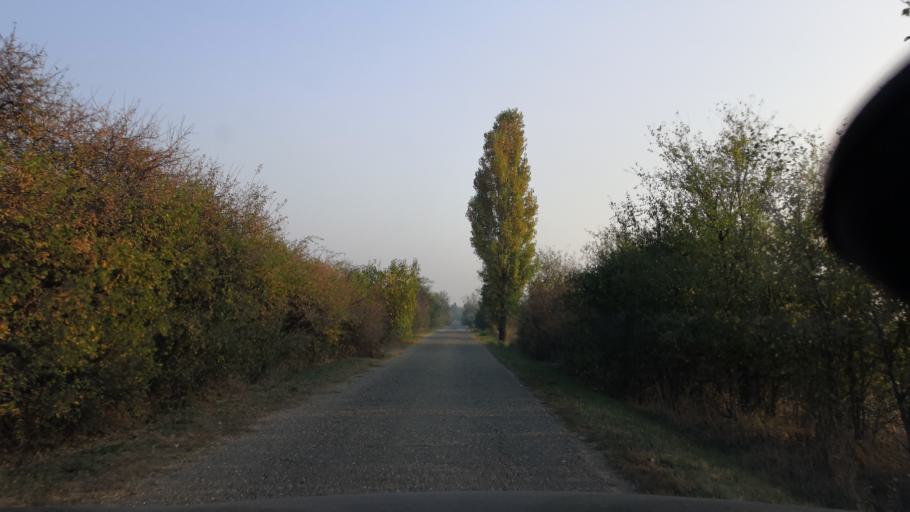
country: RS
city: Cortanovci
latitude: 45.1341
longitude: 19.9865
